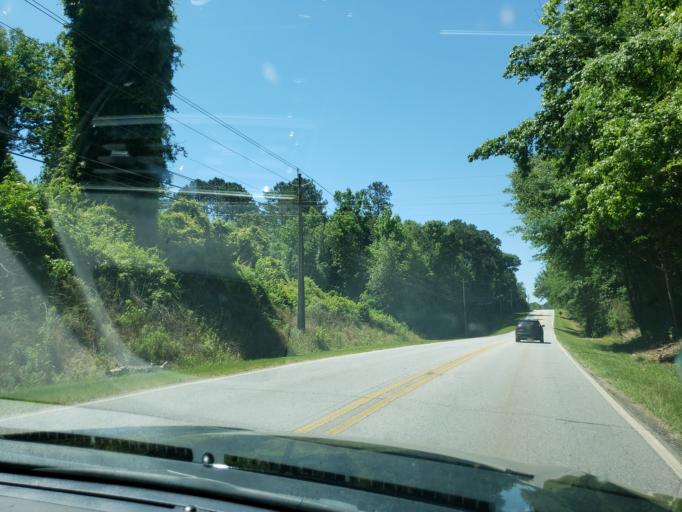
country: US
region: Alabama
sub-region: Lee County
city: Auburn
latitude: 32.6434
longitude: -85.4813
